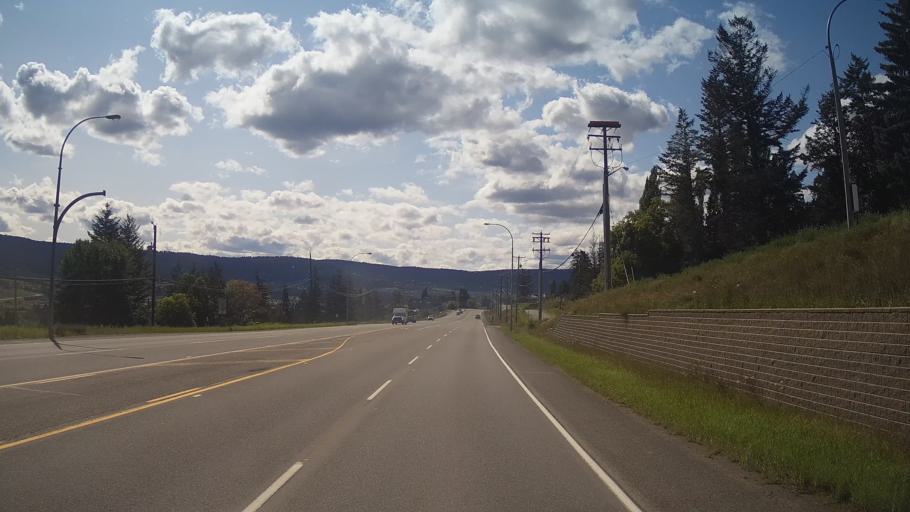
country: CA
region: British Columbia
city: Williams Lake
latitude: 52.1222
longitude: -122.1011
